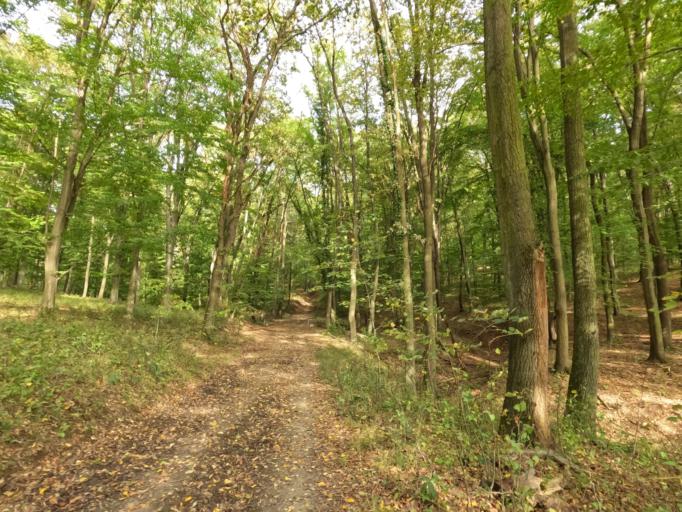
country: HU
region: Tolna
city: Szentgalpuszta
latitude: 46.3123
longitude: 18.6437
